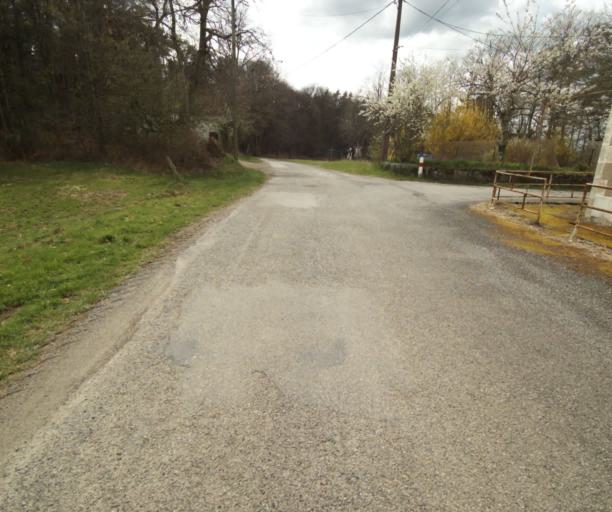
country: FR
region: Limousin
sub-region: Departement de la Correze
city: Laguenne
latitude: 45.2210
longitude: 1.8863
